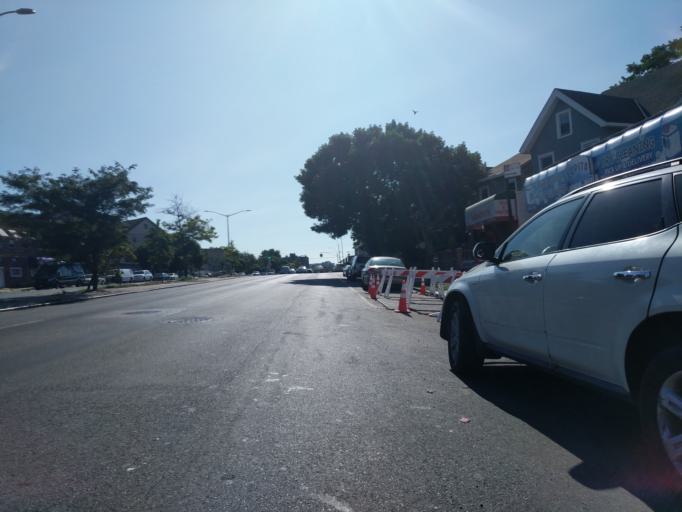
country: US
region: New York
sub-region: Queens County
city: Long Island City
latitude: 40.7613
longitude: -73.8661
